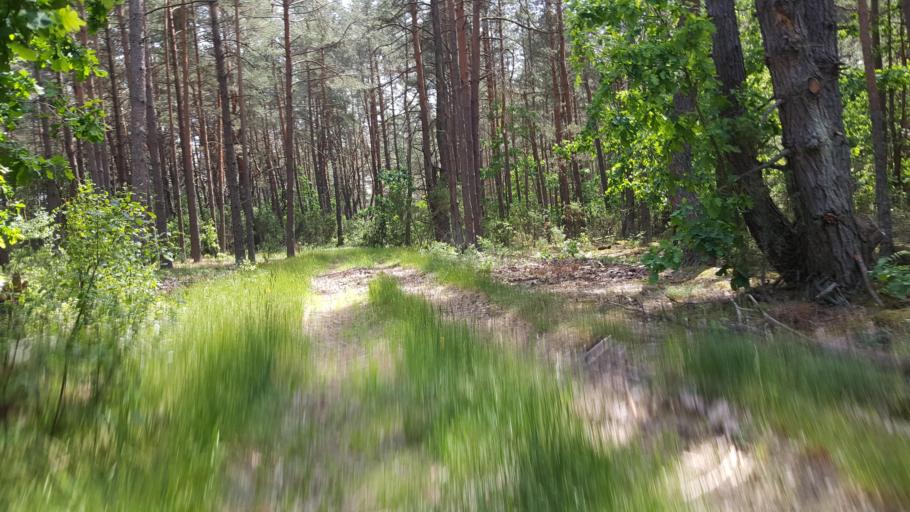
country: BY
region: Brest
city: Kamyanyuki
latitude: 52.5102
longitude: 23.8273
